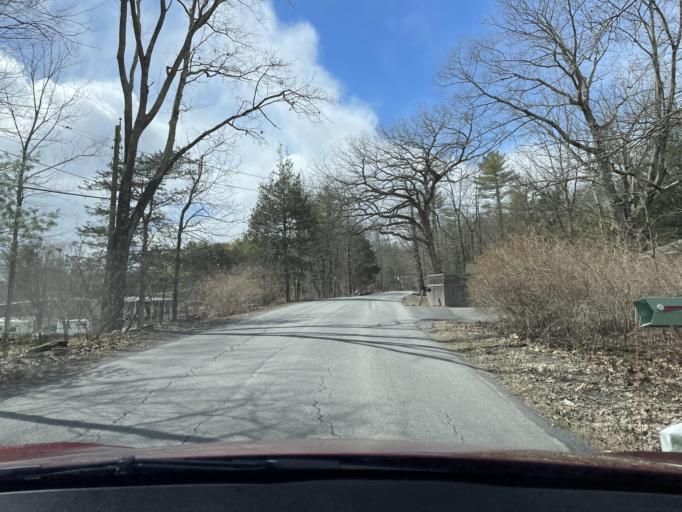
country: US
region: New York
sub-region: Ulster County
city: Zena
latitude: 42.0424
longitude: -74.0626
